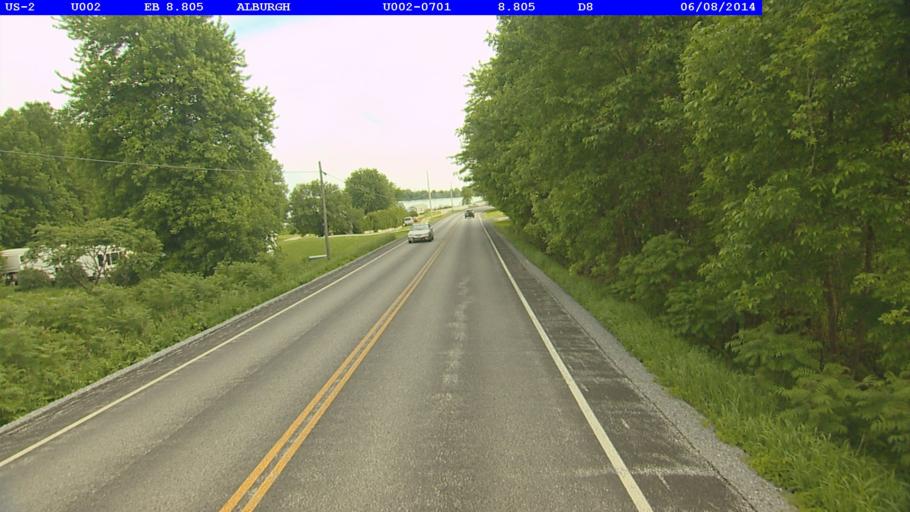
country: US
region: Vermont
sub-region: Grand Isle County
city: North Hero
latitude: 44.9237
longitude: -73.2740
